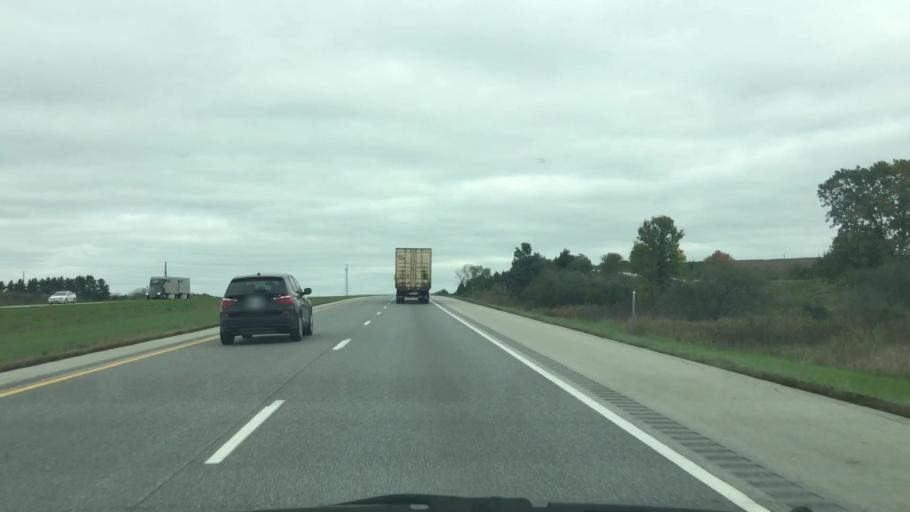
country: US
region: Iowa
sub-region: Warren County
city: Norwalk
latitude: 41.4708
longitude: -93.7789
